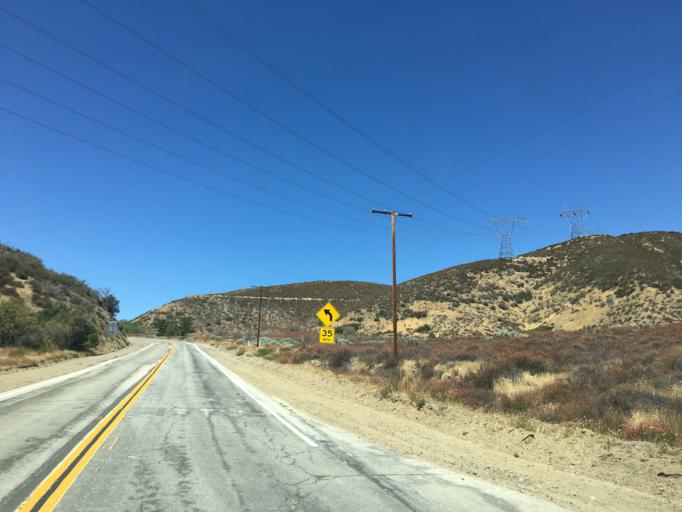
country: US
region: California
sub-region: Los Angeles County
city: Leona Valley
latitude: 34.5876
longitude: -118.3024
